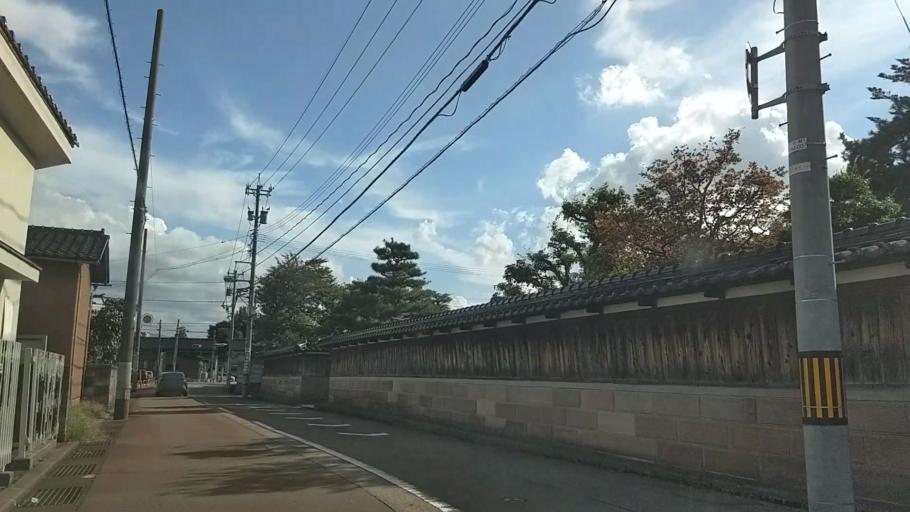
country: JP
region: Ishikawa
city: Kanazawa-shi
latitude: 36.5801
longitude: 136.6664
